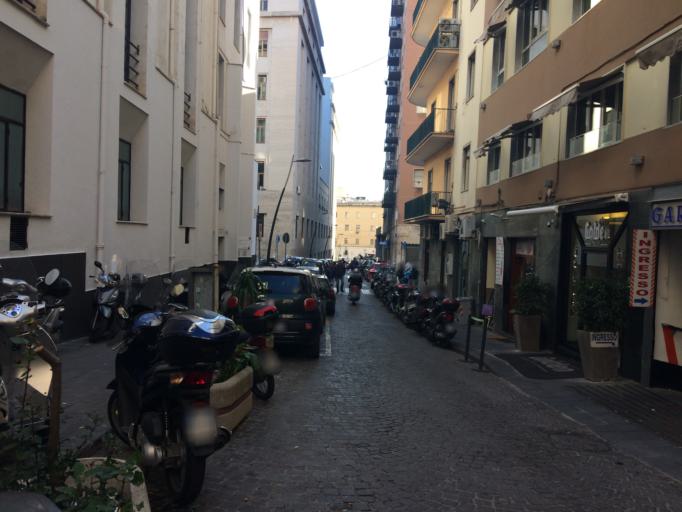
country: IT
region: Campania
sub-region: Provincia di Napoli
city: Napoli
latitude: 40.8424
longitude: 14.2508
